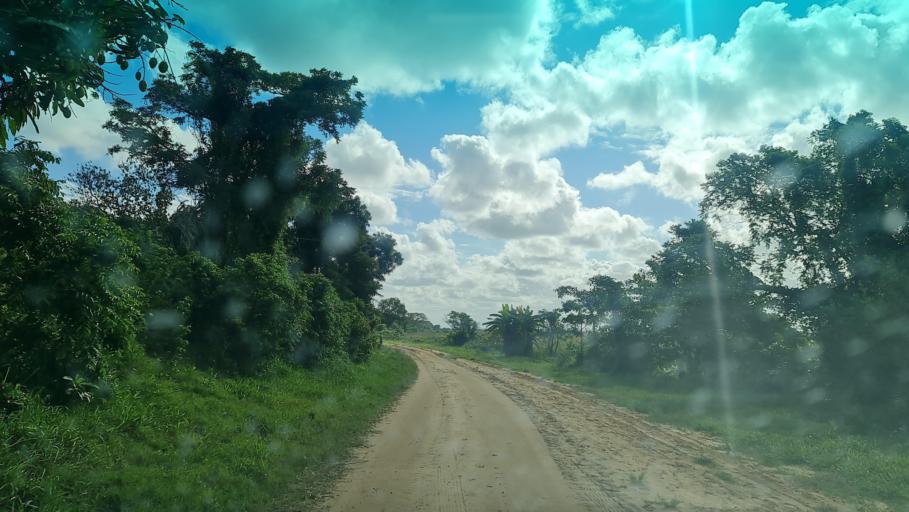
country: MZ
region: Maputo
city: Manhica
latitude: -25.4304
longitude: 32.8929
